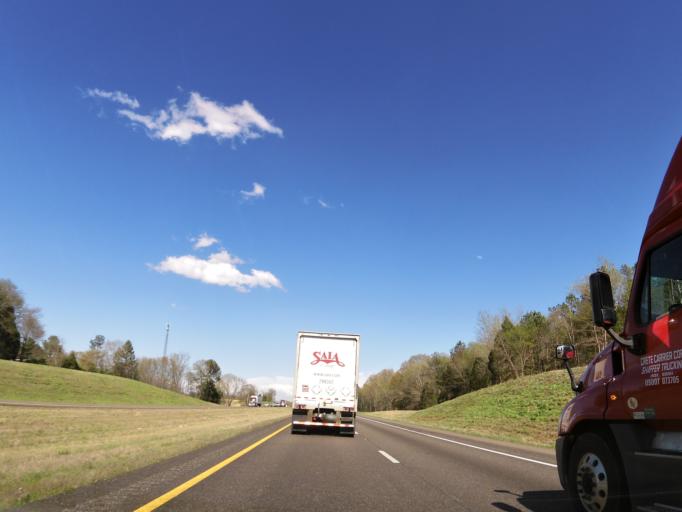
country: US
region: Tennessee
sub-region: Henderson County
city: Lexington
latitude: 35.7794
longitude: -88.4204
